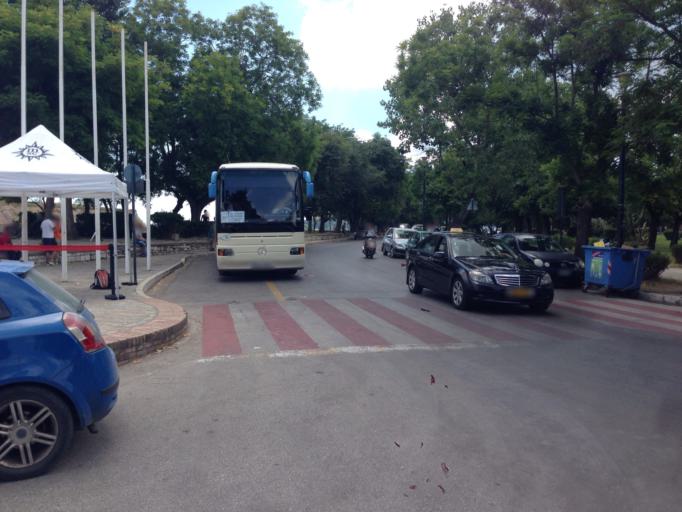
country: GR
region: Ionian Islands
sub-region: Nomos Kerkyras
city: Kerkyra
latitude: 39.6234
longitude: 19.9256
